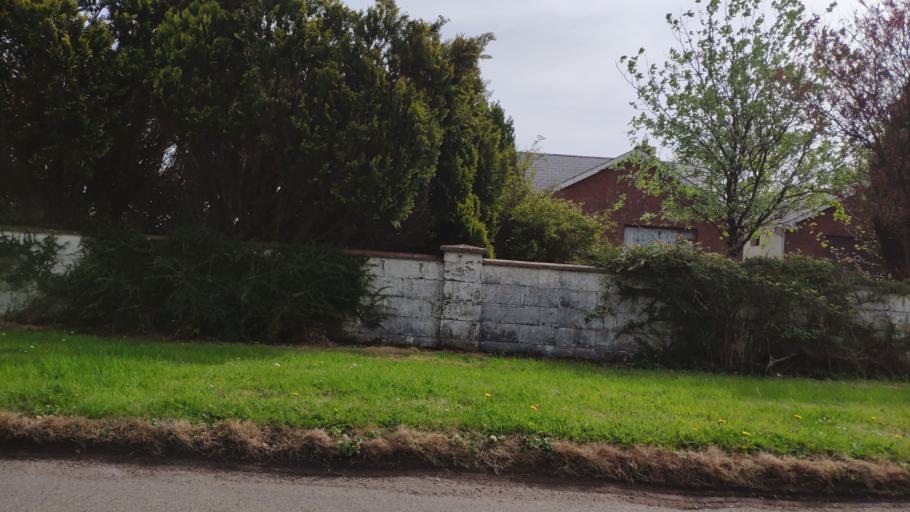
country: IE
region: Munster
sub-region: County Cork
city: Blarney
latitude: 51.9713
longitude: -8.5131
